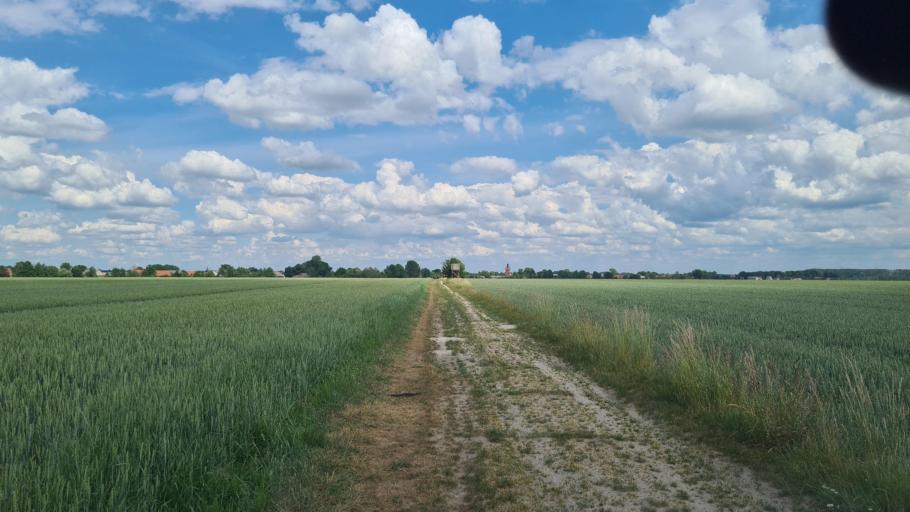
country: DE
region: Brandenburg
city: Doberlug-Kirchhain
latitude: 51.6483
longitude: 13.5173
